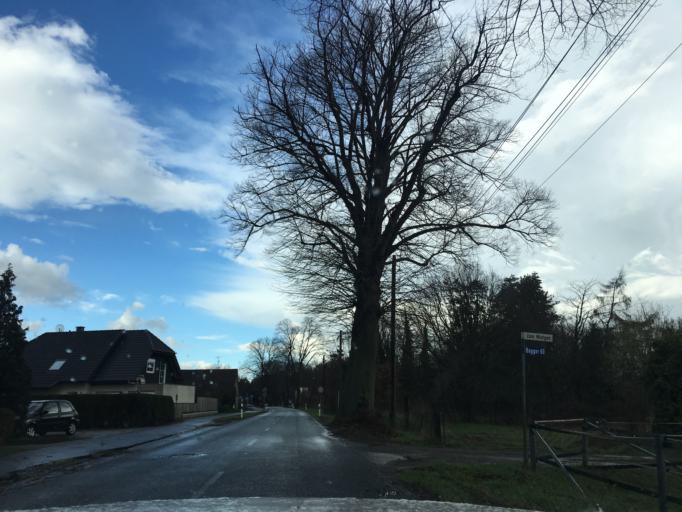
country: DE
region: North Rhine-Westphalia
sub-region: Regierungsbezirk Munster
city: Isselburg
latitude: 51.7818
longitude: 6.4647
